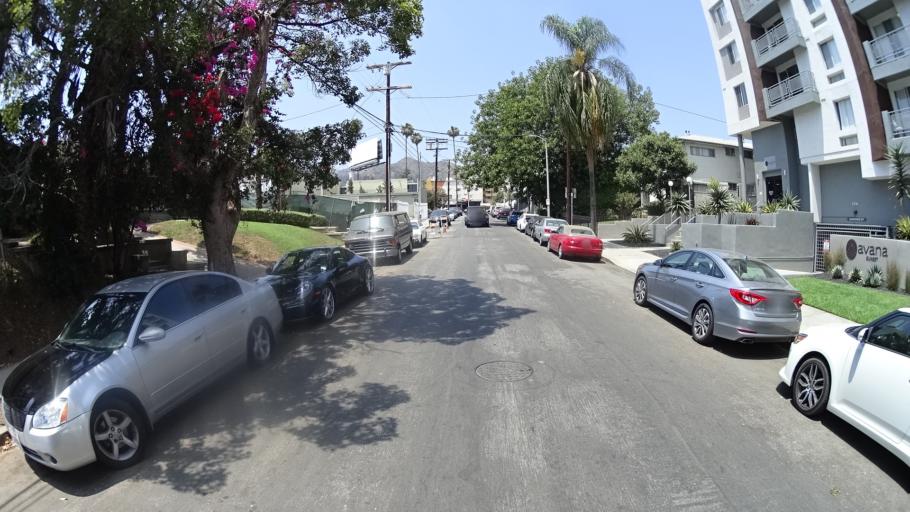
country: US
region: California
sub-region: Los Angeles County
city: West Hollywood
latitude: 34.0970
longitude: -118.3504
